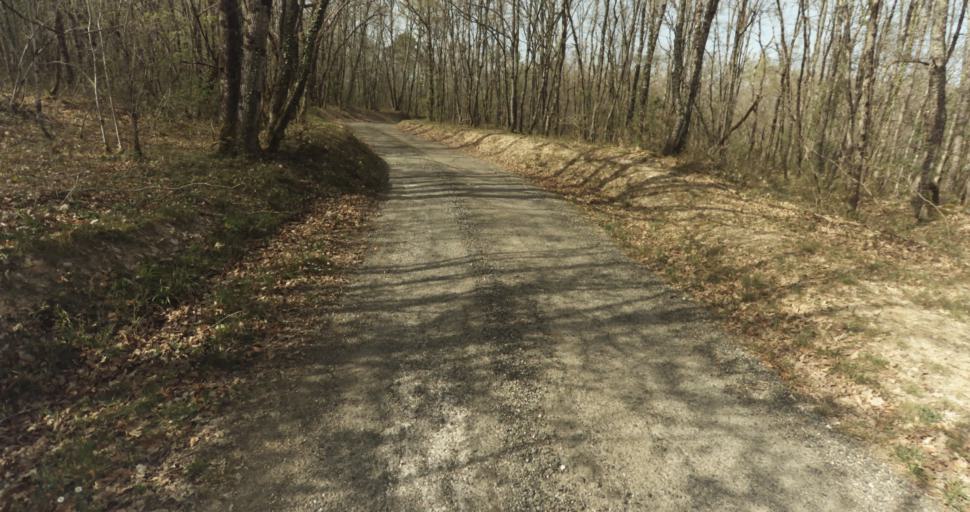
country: FR
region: Midi-Pyrenees
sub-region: Departement du Tarn-et-Garonne
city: Lafrancaise
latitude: 44.1525
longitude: 1.1765
